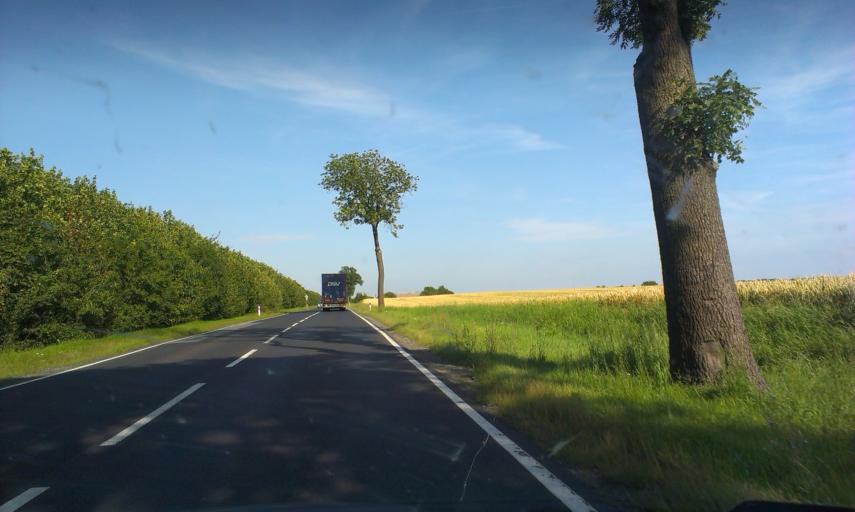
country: PL
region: Kujawsko-Pomorskie
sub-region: Powiat nakielski
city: Sadki
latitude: 53.1521
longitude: 17.4913
